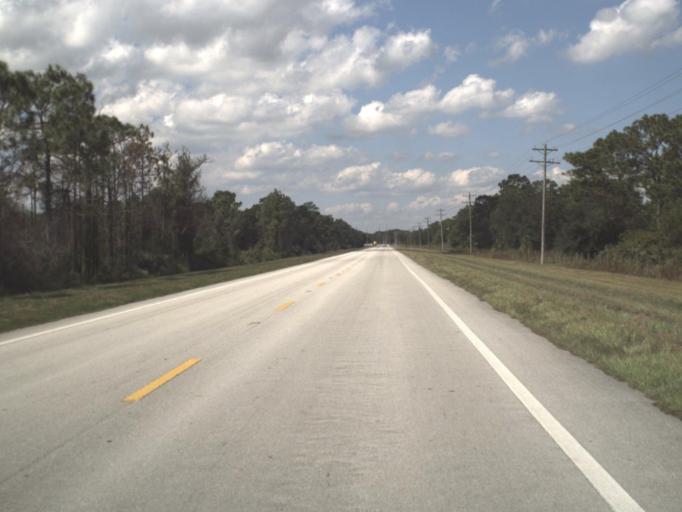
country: US
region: Florida
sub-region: Okeechobee County
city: Okeechobee
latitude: 27.3881
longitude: -81.0206
